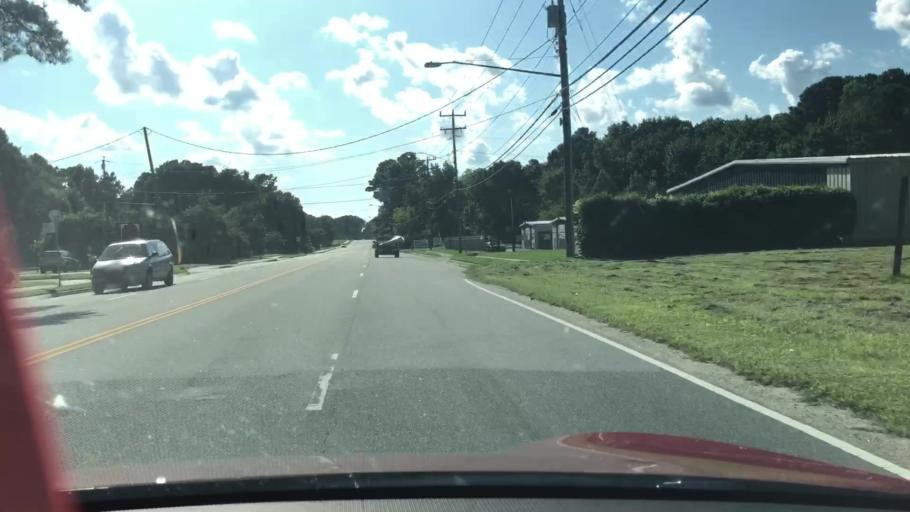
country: US
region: Virginia
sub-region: City of Virginia Beach
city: Virginia Beach
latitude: 36.8427
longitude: -76.0061
